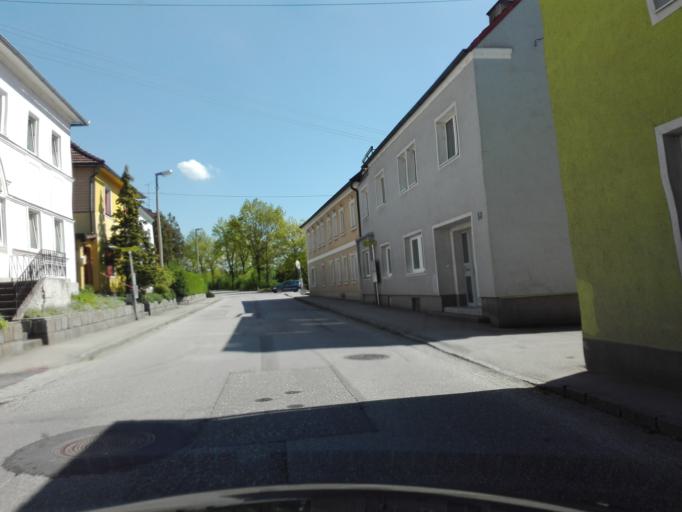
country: AT
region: Upper Austria
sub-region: Politischer Bezirk Grieskirchen
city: Bad Schallerbach
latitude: 48.3144
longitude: 13.9048
